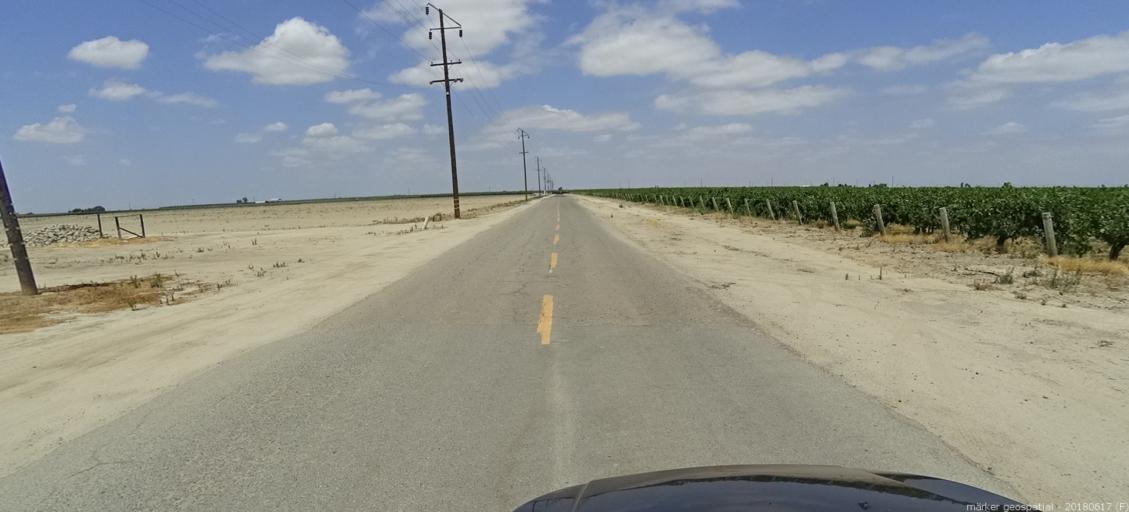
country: US
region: California
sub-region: Fresno County
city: Biola
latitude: 36.8307
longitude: -120.1151
